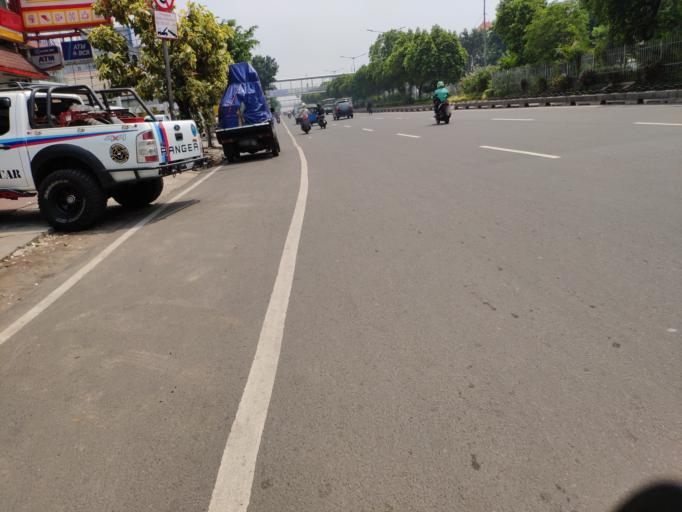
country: ID
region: Jakarta Raya
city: Jakarta
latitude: -6.2058
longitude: 106.8584
